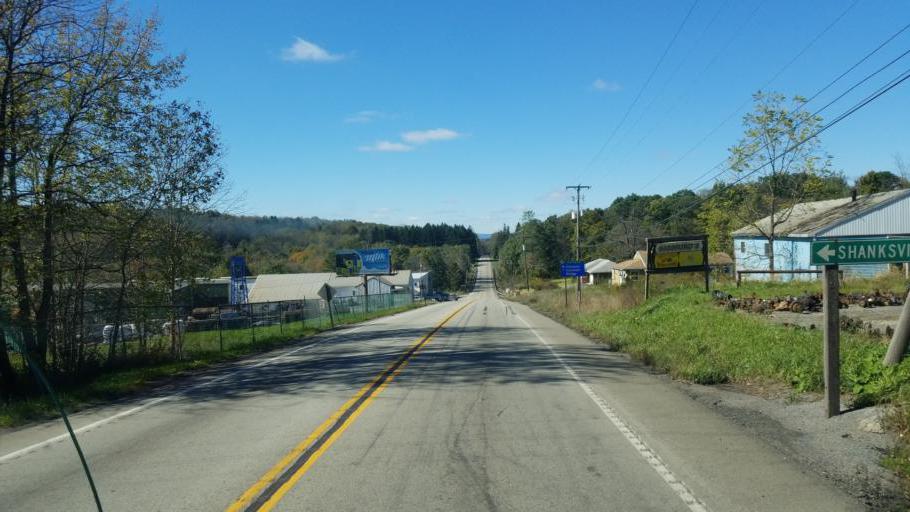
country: US
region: Pennsylvania
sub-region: Somerset County
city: Friedens
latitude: 40.0882
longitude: -78.9106
